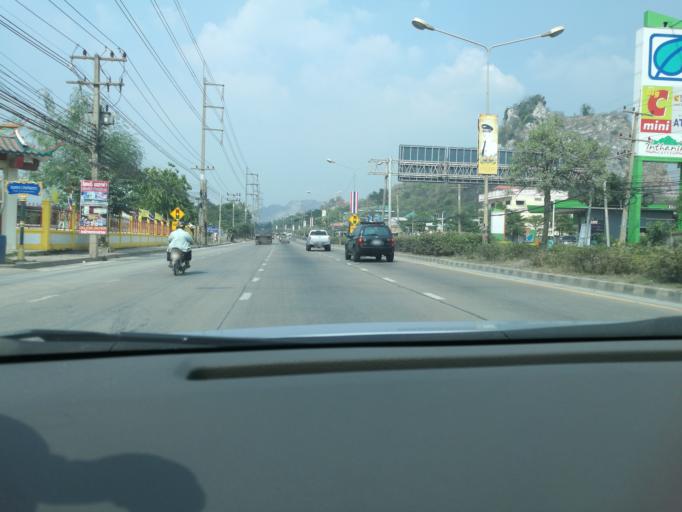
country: TH
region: Sara Buri
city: Phra Phutthabat
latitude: 14.6938
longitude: 100.8674
